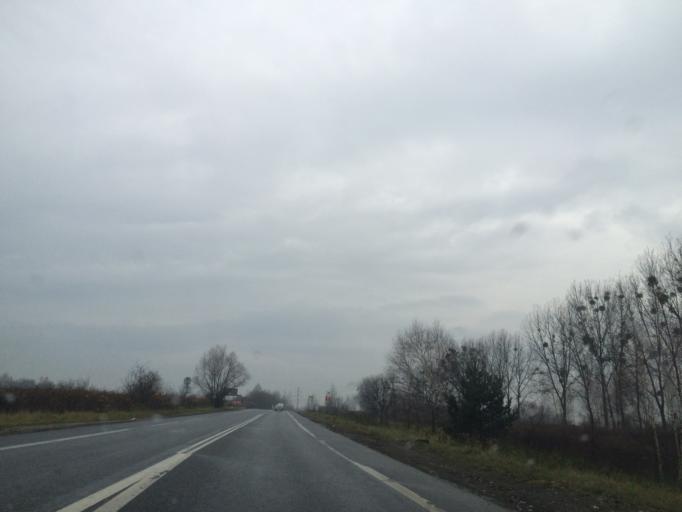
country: PL
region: Silesian Voivodeship
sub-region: Piekary Slaskie
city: Piekary Slaskie
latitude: 50.3687
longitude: 18.9122
